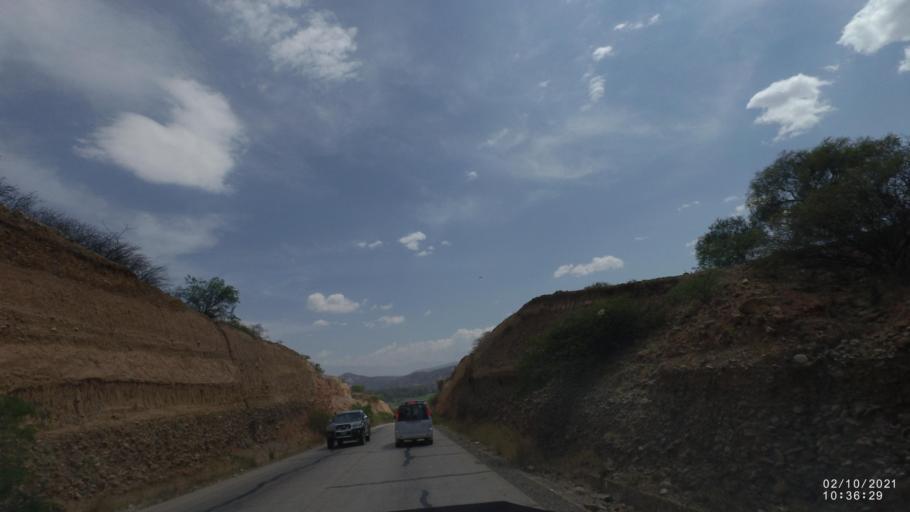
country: BO
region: Cochabamba
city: Capinota
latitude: -17.6501
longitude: -66.2585
